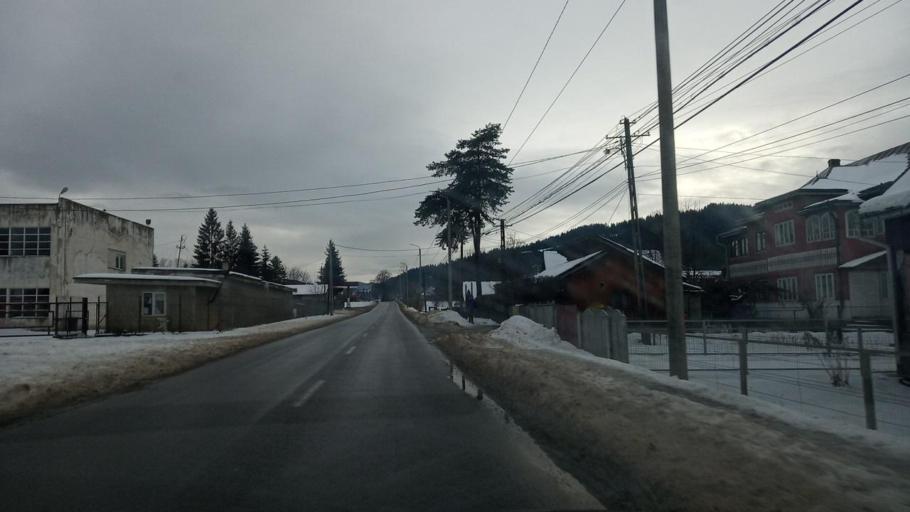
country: RO
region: Suceava
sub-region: Comuna Frasin
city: Frasin
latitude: 47.5310
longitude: 25.7981
